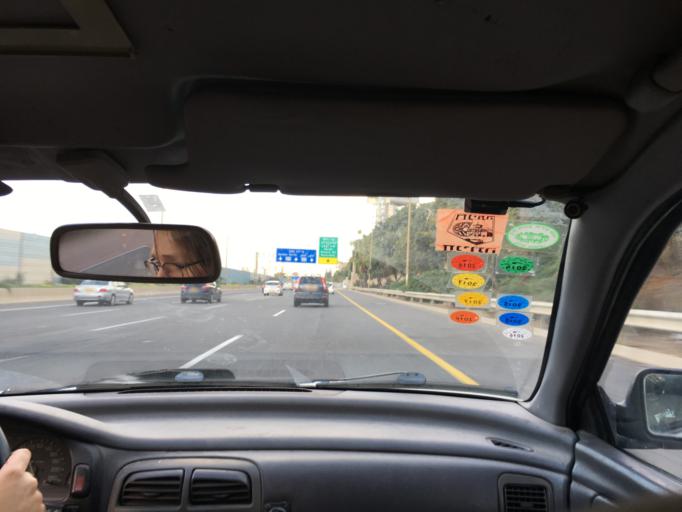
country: IL
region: Tel Aviv
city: Ramat Gan
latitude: 32.0900
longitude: 34.8009
